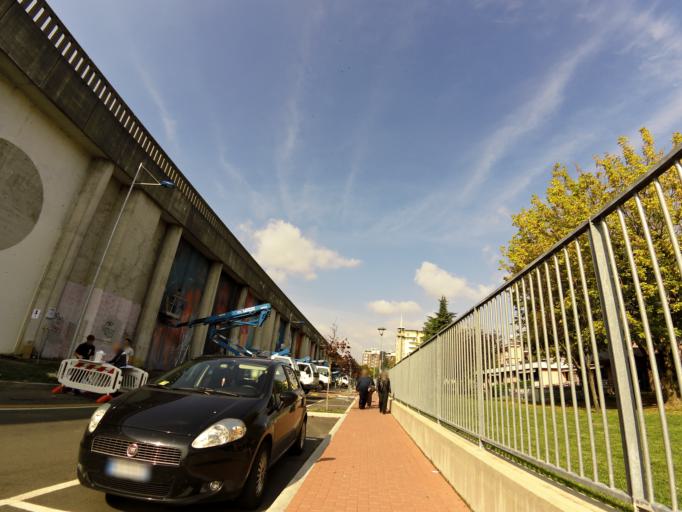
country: IT
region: Lombardy
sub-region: Citta metropolitana di Milano
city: Civesio
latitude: 45.4060
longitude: 9.2690
